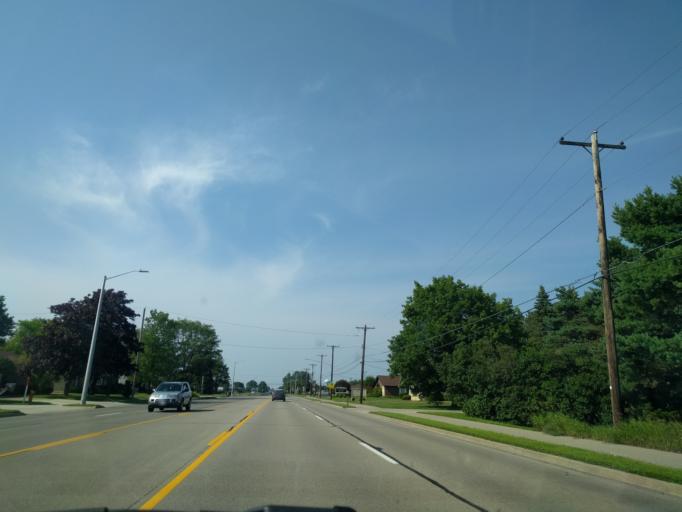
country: US
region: Michigan
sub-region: Delta County
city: Escanaba
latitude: 45.7328
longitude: -87.0800
